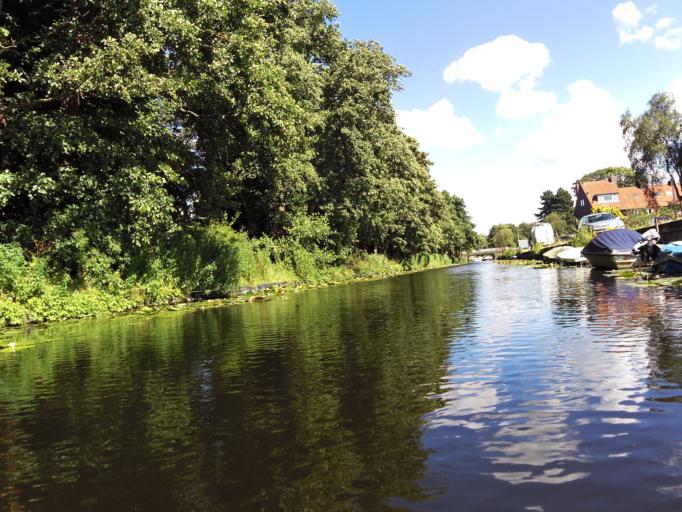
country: NL
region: South Holland
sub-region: Gemeente Wassenaar
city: Wassenaar
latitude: 52.1451
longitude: 4.4006
